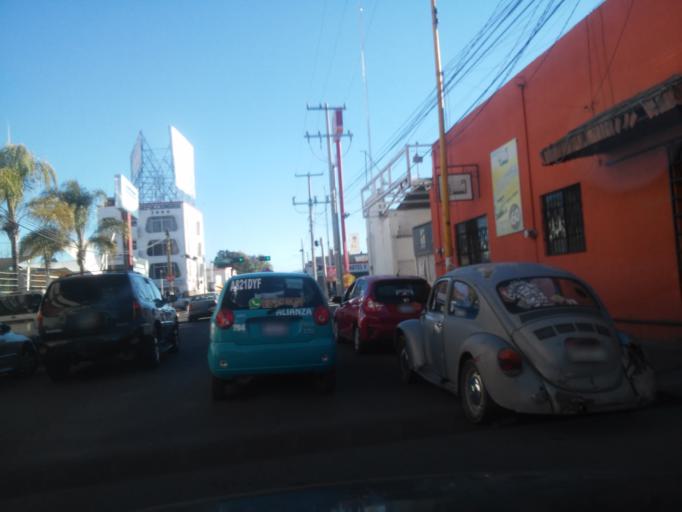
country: MX
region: Durango
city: Victoria de Durango
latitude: 24.0292
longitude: -104.6473
